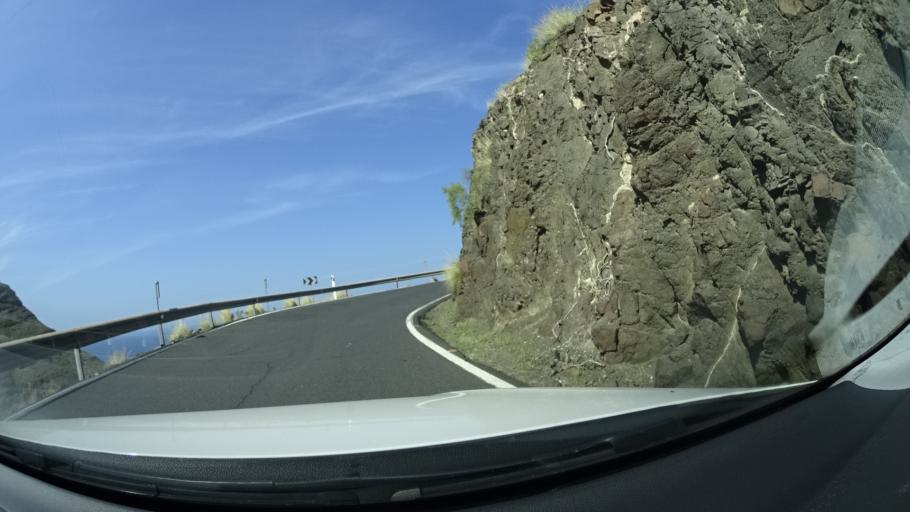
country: ES
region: Canary Islands
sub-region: Provincia de Las Palmas
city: Agaete
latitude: 28.0851
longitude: -15.7048
